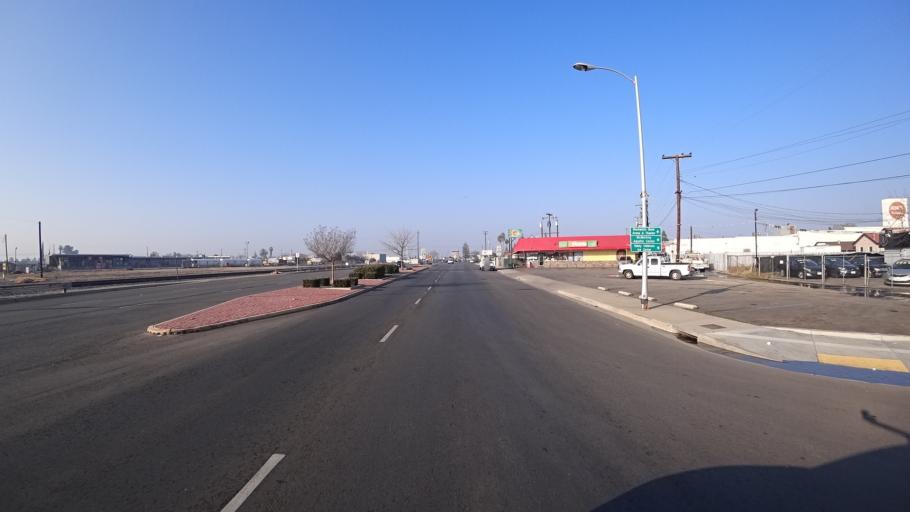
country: US
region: California
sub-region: Kern County
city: Bakersfield
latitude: 35.3735
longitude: -118.9957
